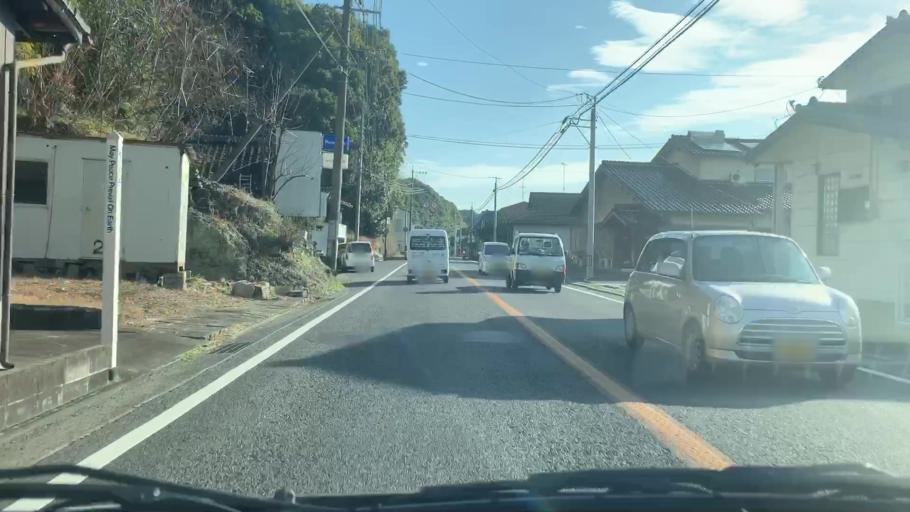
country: JP
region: Saga Prefecture
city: Takeocho-takeo
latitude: 33.2169
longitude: 130.0812
